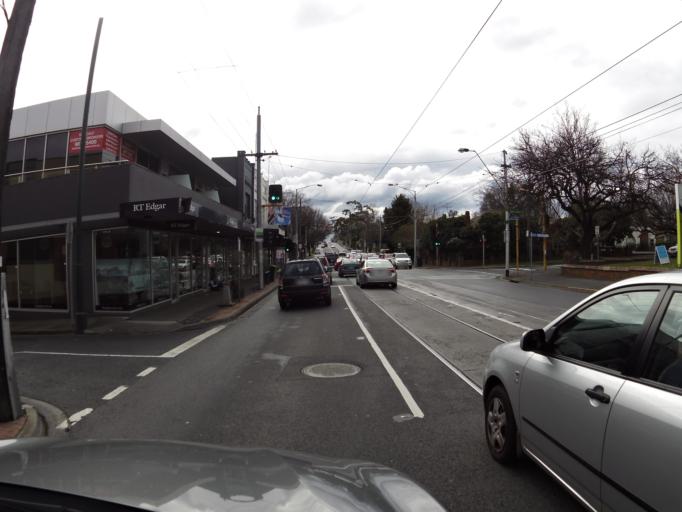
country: AU
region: Victoria
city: Balwyn
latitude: -37.8162
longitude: 145.0595
